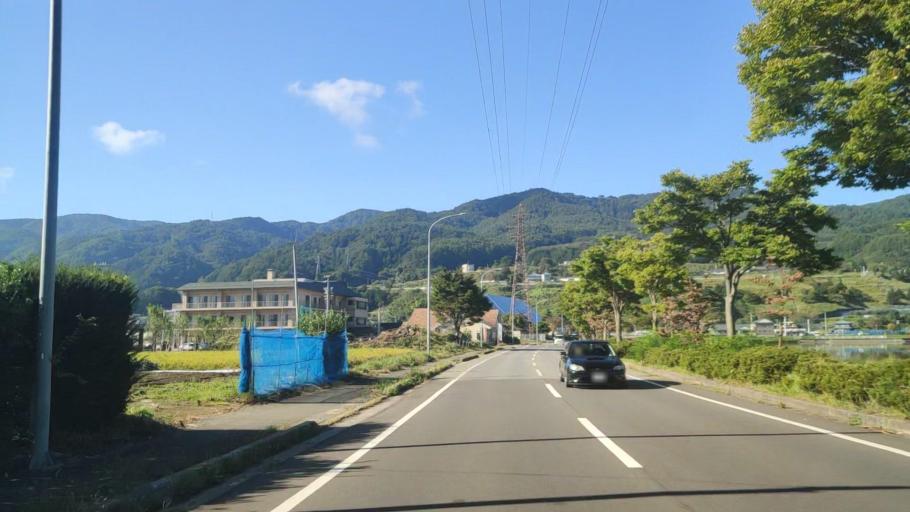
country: JP
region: Nagano
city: Suwa
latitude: 36.0307
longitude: 138.0822
